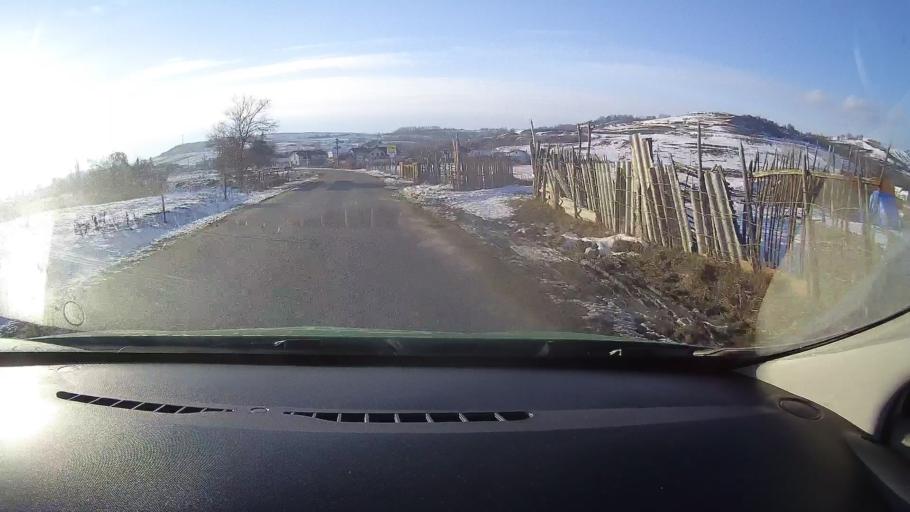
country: RO
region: Sibiu
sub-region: Oras Agnita
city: Ruja
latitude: 45.9837
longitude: 24.6504
